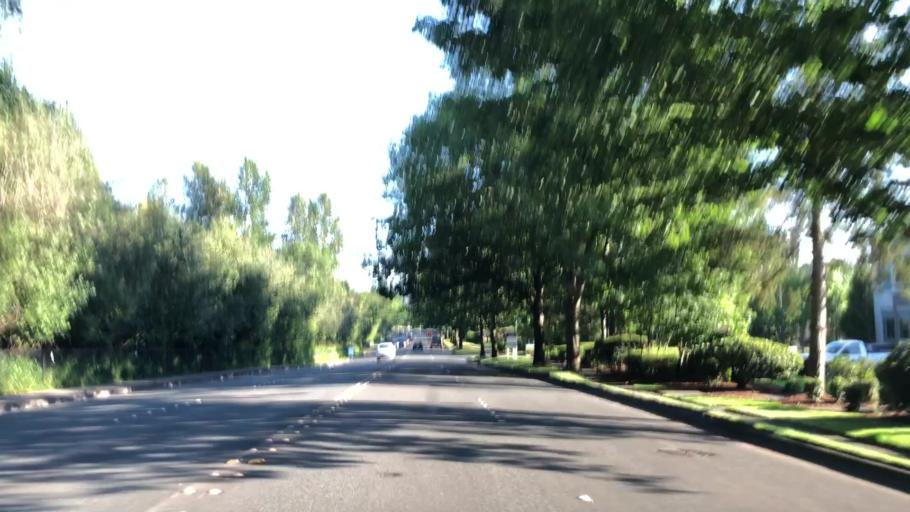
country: US
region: Washington
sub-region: King County
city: Woodinville
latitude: 47.7720
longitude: -122.1802
